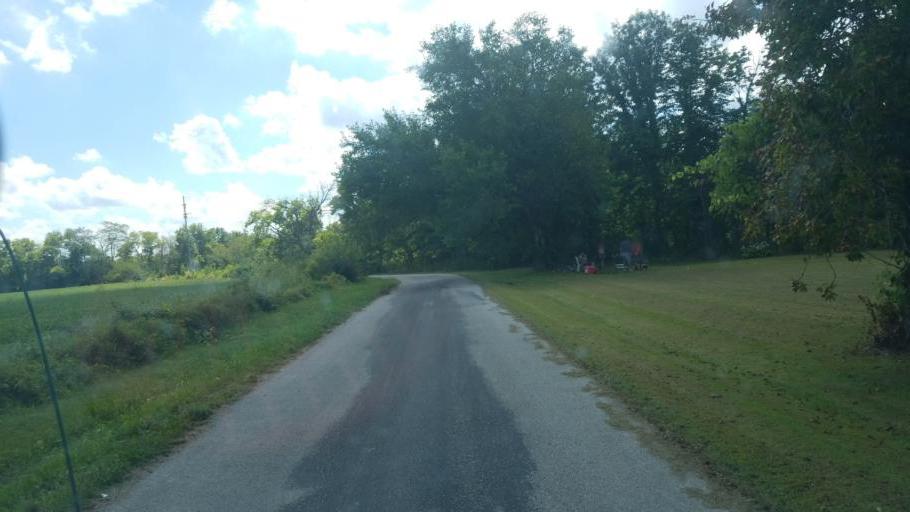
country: US
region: Ohio
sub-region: Marion County
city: Prospect
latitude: 40.4421
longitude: -83.1907
